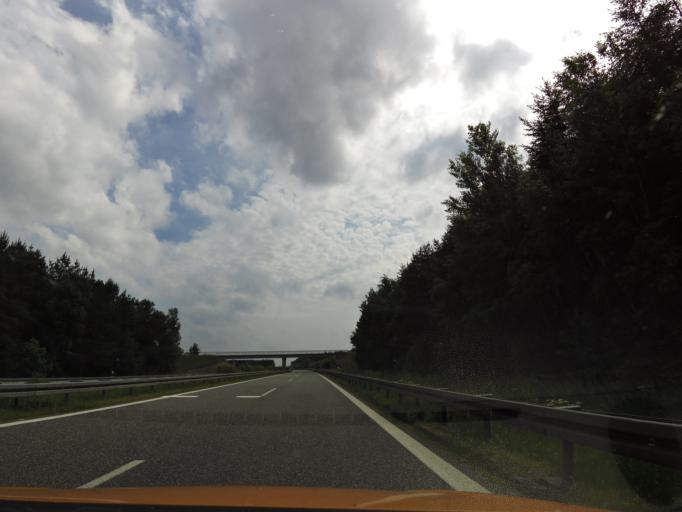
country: DE
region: Mecklenburg-Vorpommern
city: Mirow
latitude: 53.4958
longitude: 11.4769
